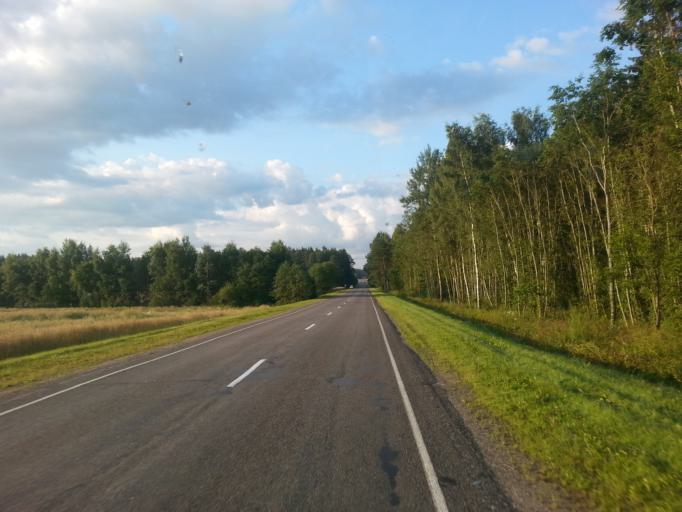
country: BY
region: Minsk
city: Kryvichy
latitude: 54.6137
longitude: 27.1764
